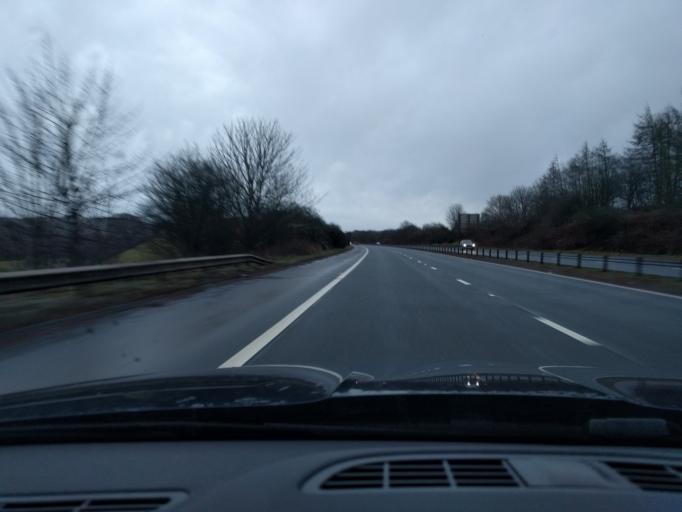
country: GB
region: Scotland
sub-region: Falkirk
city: Polmont
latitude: 55.9867
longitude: -3.6638
